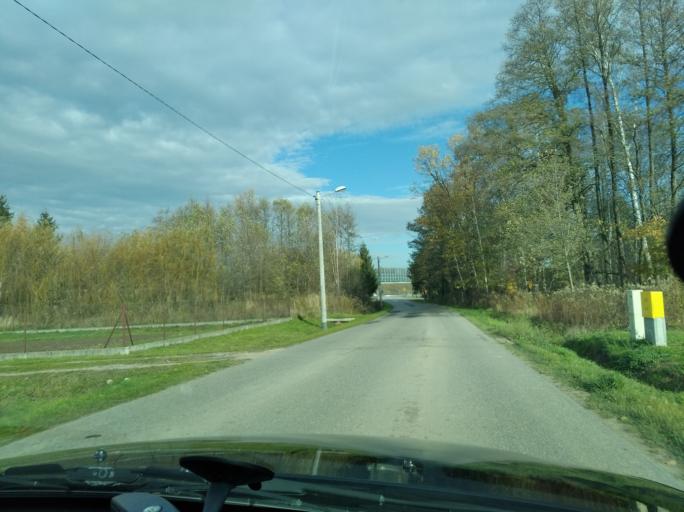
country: PL
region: Subcarpathian Voivodeship
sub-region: Powiat ropczycko-sedziszowski
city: Sedziszow Malopolski
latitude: 50.1077
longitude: 21.6856
